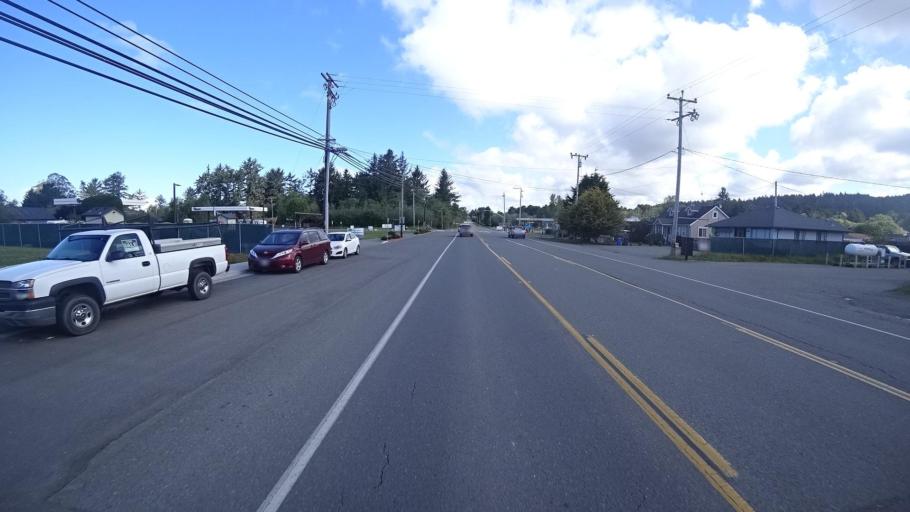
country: US
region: California
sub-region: Humboldt County
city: McKinleyville
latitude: 40.9552
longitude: -124.1010
